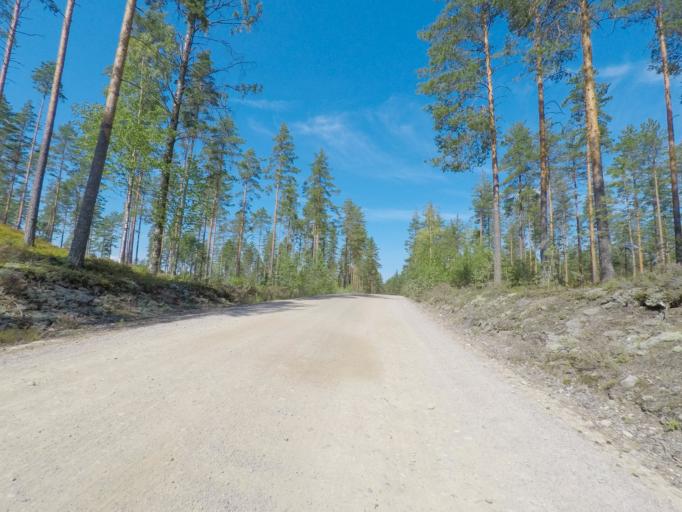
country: FI
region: Southern Savonia
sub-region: Mikkeli
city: Puumala
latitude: 61.4159
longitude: 28.0435
